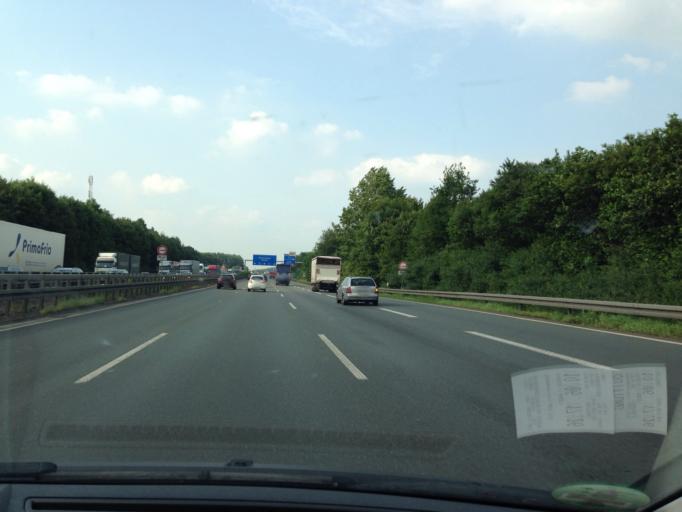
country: DE
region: North Rhine-Westphalia
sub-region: Regierungsbezirk Arnsberg
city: Holzwickede
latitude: 51.5092
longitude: 7.6521
